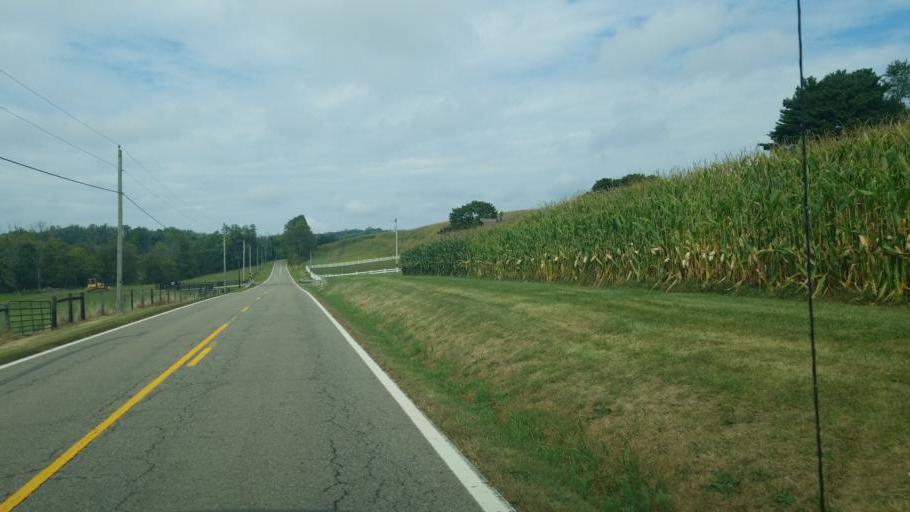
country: US
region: Ohio
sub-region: Perry County
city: Thornport
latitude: 39.9678
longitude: -82.2667
